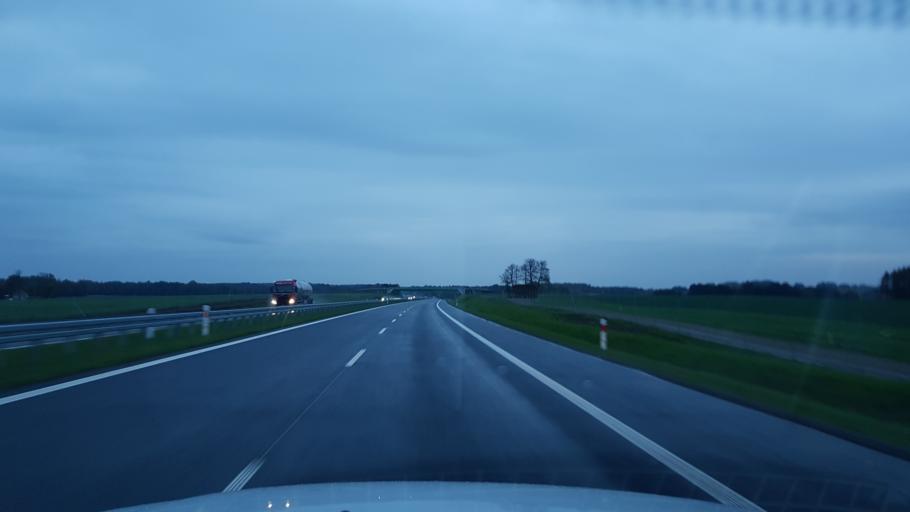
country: PL
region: West Pomeranian Voivodeship
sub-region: Powiat gryficki
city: Brojce
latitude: 53.9211
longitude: 15.3847
